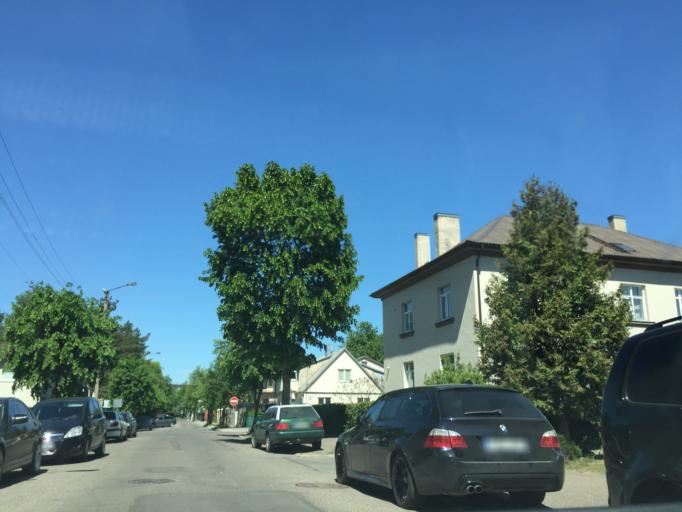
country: LT
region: Panevezys
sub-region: Panevezys City
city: Panevezys
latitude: 55.7244
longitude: 24.3722
